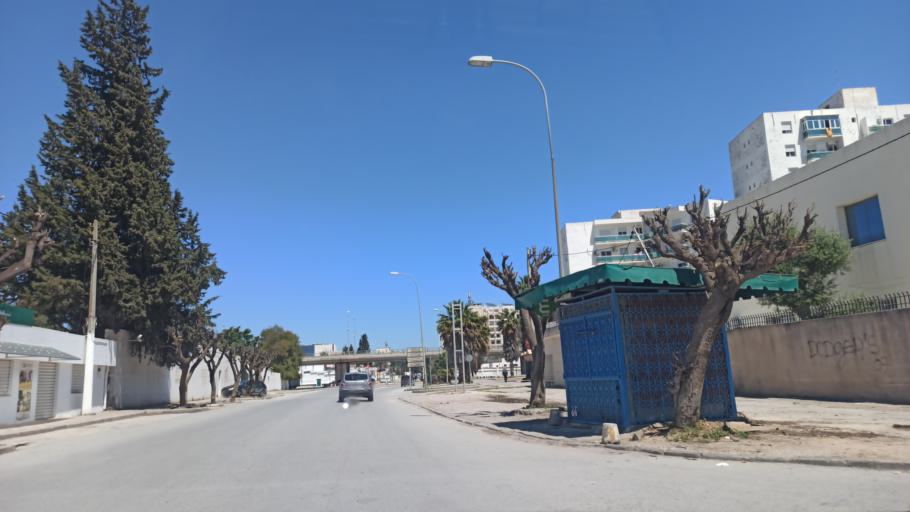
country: TN
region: Tunis
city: Tunis
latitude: 36.8295
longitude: 10.1860
